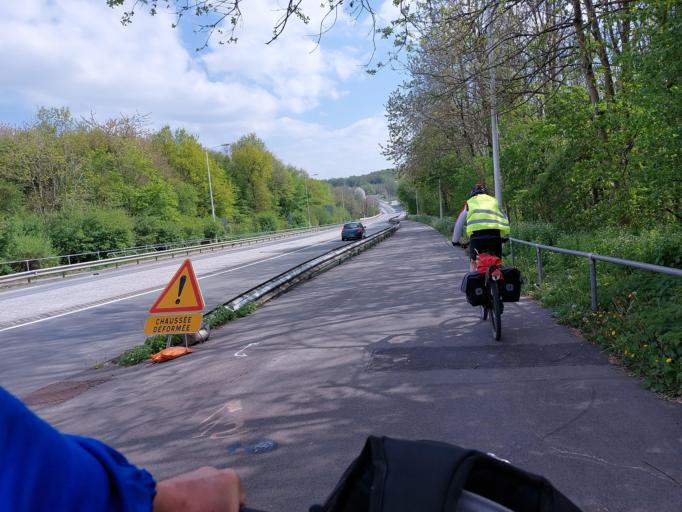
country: FR
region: Nord-Pas-de-Calais
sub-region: Departement du Nord
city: Hautmont
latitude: 50.2509
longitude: 3.9000
